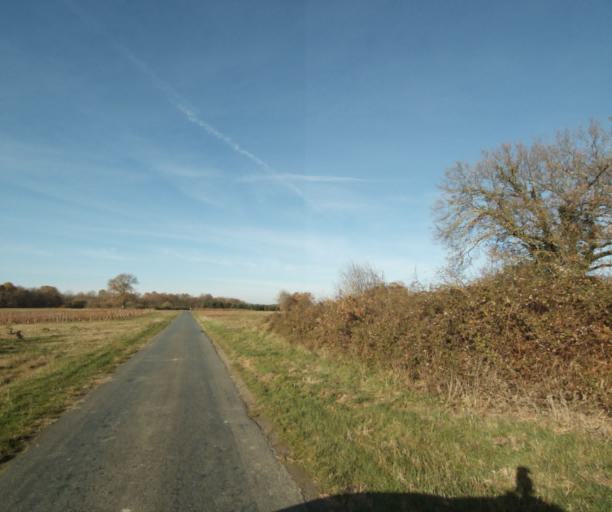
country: FR
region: Poitou-Charentes
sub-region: Departement de la Charente-Maritime
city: Cherac
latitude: 45.7443
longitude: -0.4697
